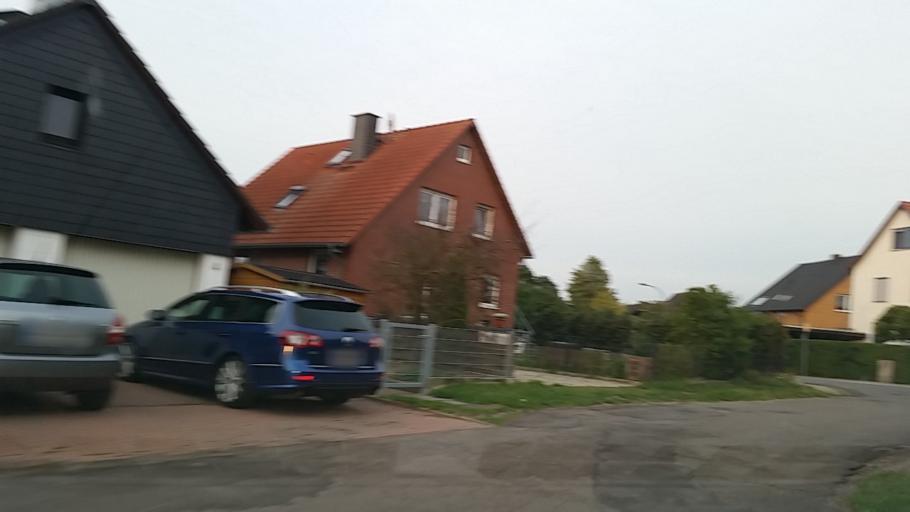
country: DE
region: Lower Saxony
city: Vordorf
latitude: 52.3578
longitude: 10.4959
